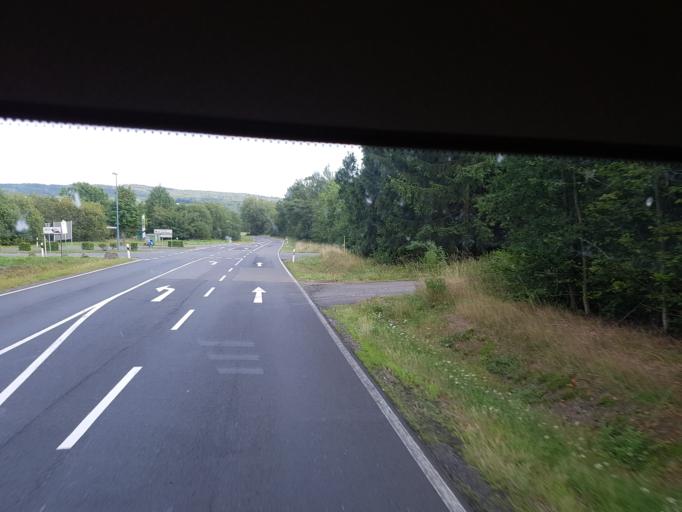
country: DE
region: Rheinland-Pfalz
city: Kradenbach
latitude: 50.2446
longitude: 6.8394
